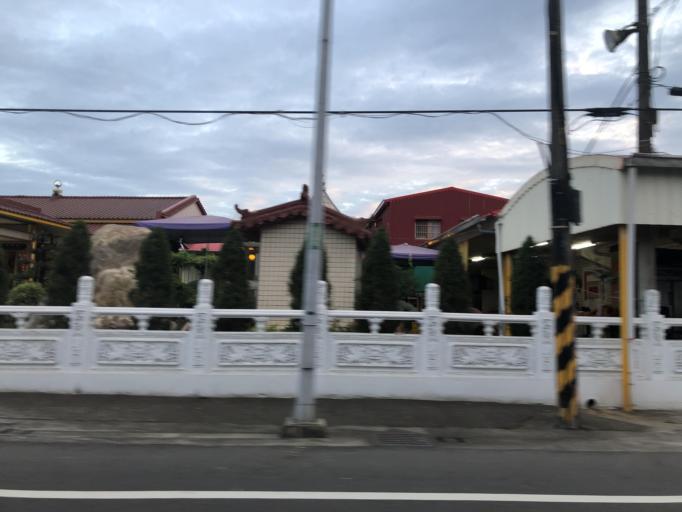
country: TW
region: Taiwan
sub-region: Tainan
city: Tainan
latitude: 23.0254
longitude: 120.3412
